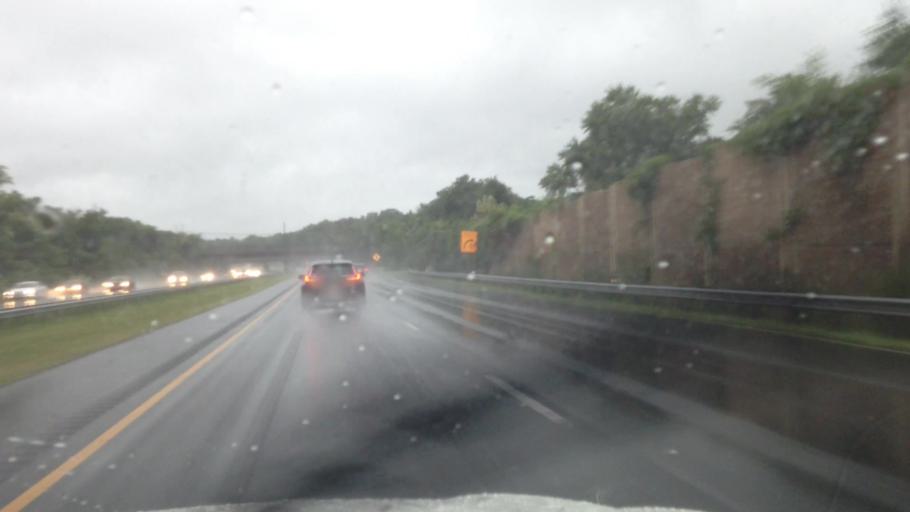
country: US
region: Maryland
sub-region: Prince George's County
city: Landover
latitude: 38.9323
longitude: -76.8950
